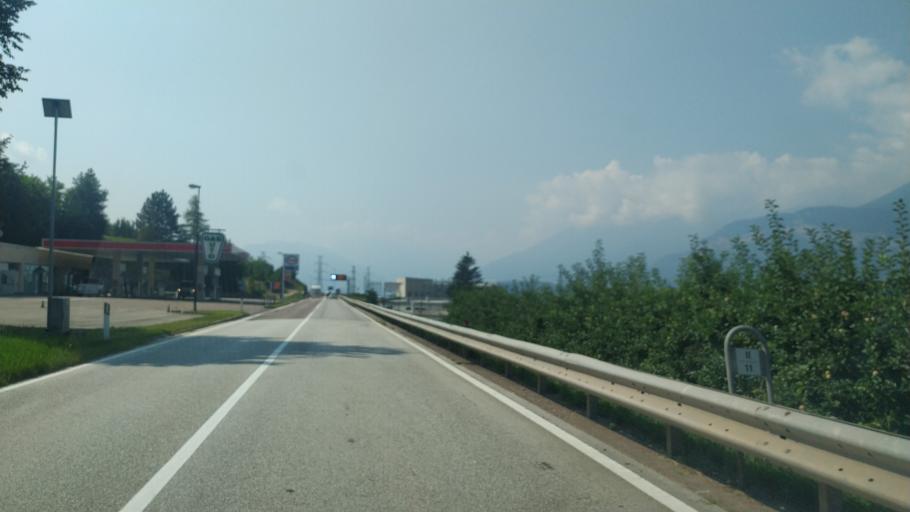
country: IT
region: Trentino-Alto Adige
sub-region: Provincia di Trento
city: Taio
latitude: 46.3301
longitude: 11.0640
